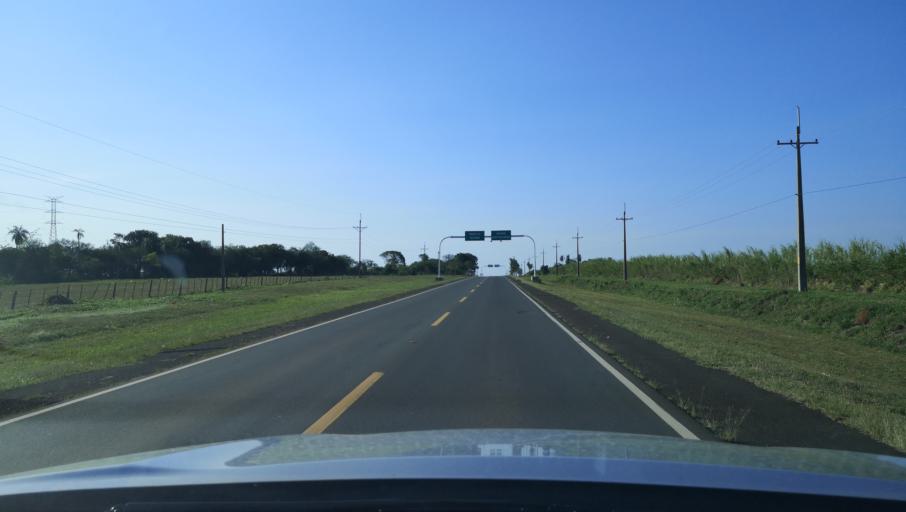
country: PY
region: Misiones
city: Santa Maria
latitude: -26.7859
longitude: -57.0261
